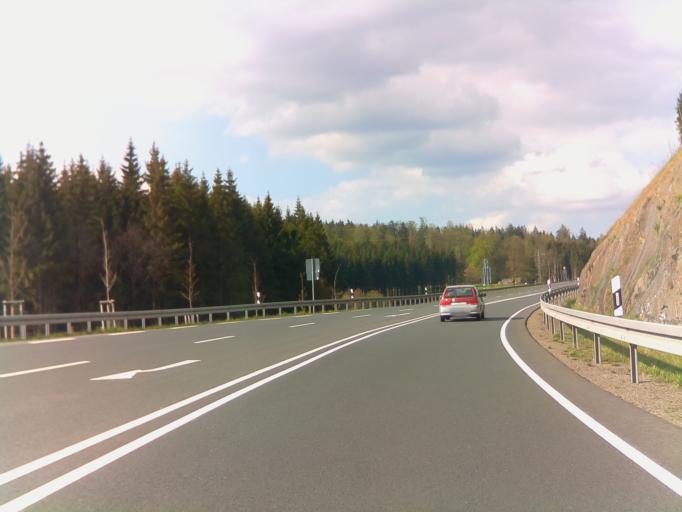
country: DE
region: Bavaria
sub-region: Upper Franconia
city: Teuschnitz
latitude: 50.4180
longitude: 11.3536
